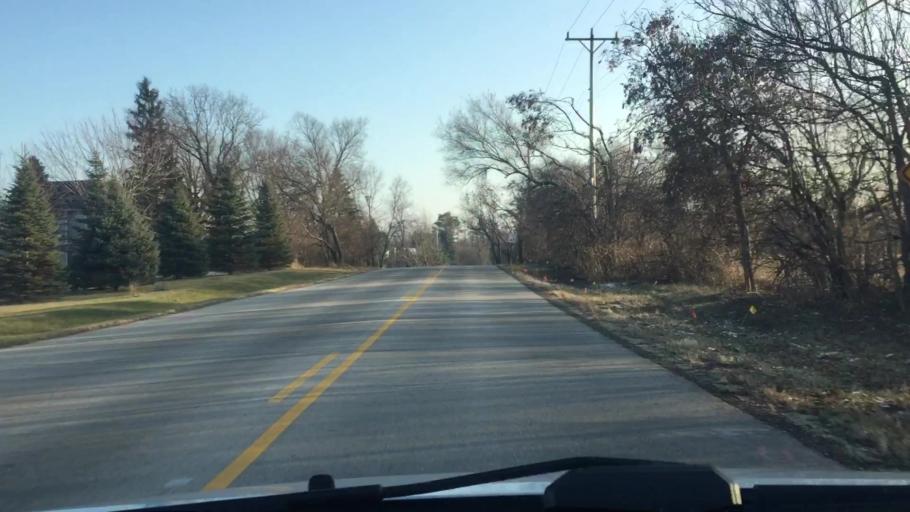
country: US
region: Wisconsin
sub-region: Waukesha County
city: Dousman
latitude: 43.0343
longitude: -88.4813
